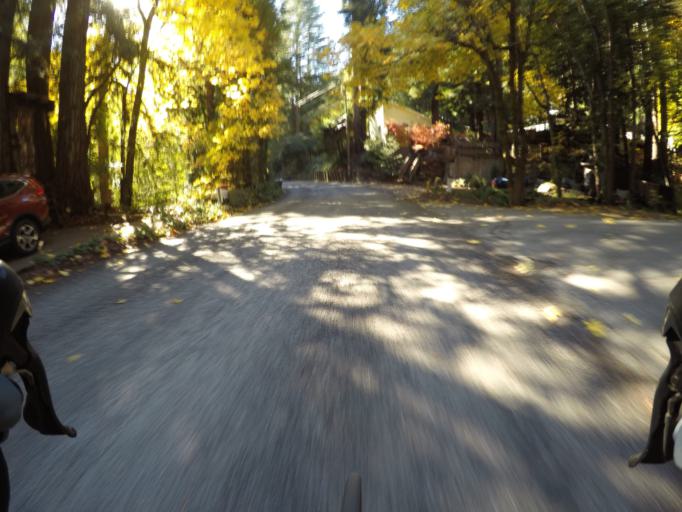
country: US
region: California
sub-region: Santa Cruz County
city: Lompico
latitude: 37.1000
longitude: -122.0360
